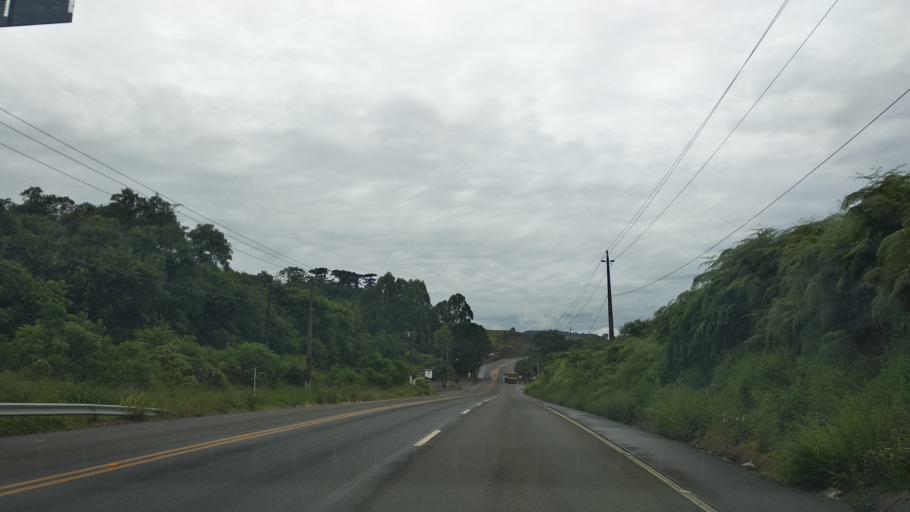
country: BR
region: Santa Catarina
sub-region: Videira
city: Videira
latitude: -27.0350
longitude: -51.1544
